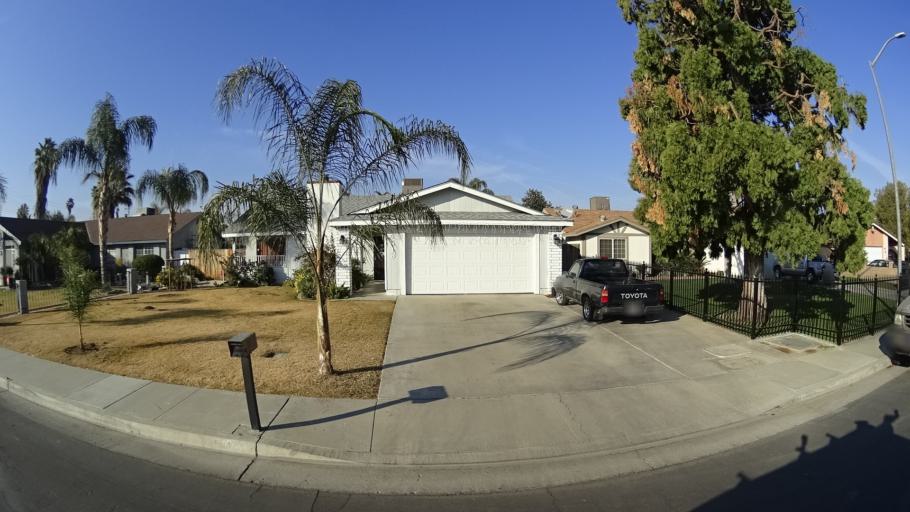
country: US
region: California
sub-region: Kern County
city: Greenfield
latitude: 35.3134
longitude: -119.0084
